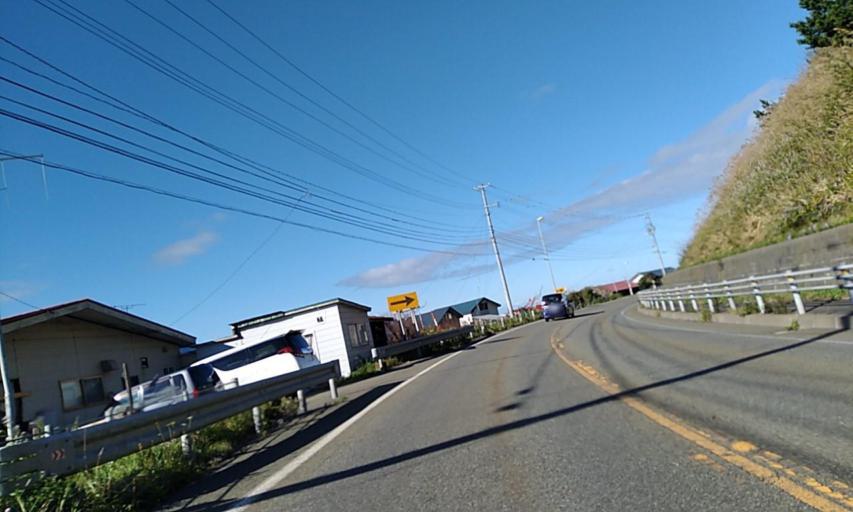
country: JP
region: Hokkaido
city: Shizunai-furukawacho
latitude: 42.2665
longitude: 142.4963
